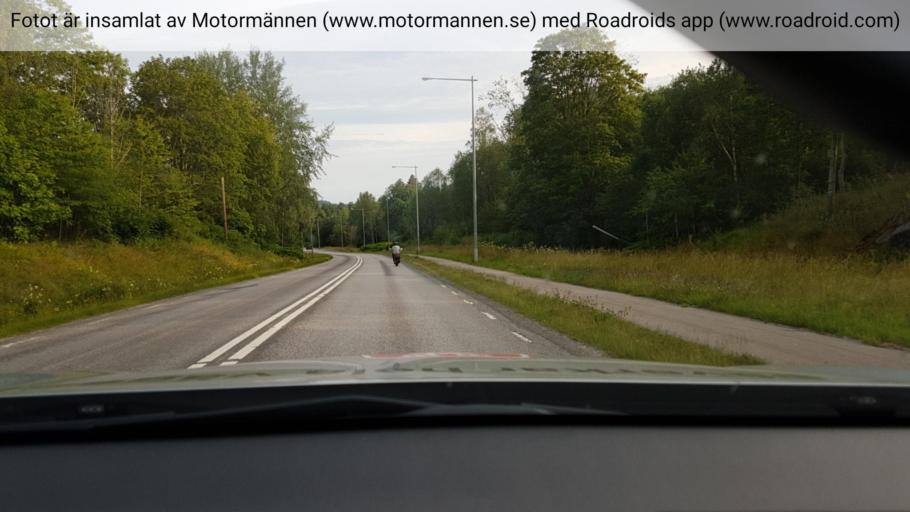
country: SE
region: Vaestra Goetaland
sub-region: Uddevalla Kommun
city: Uddevalla
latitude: 58.3640
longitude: 11.9668
